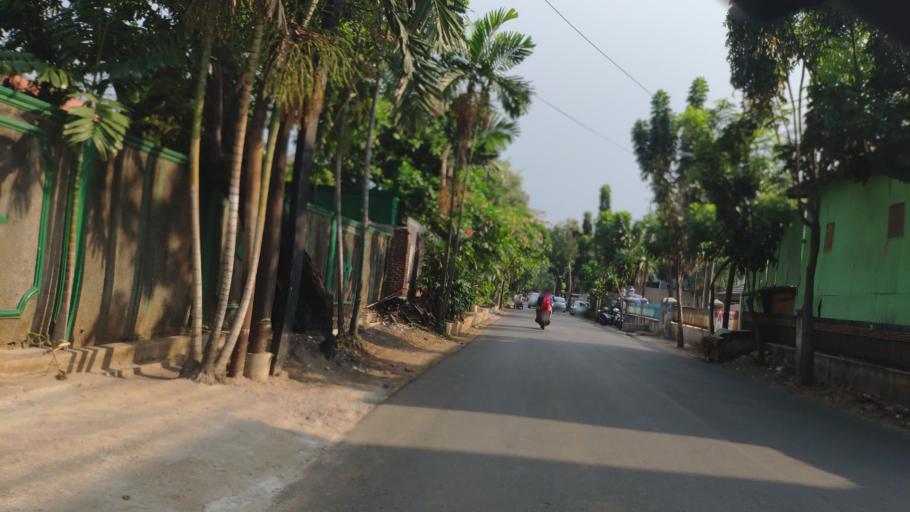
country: ID
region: Banten
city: South Tangerang
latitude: -6.2830
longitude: 106.7995
